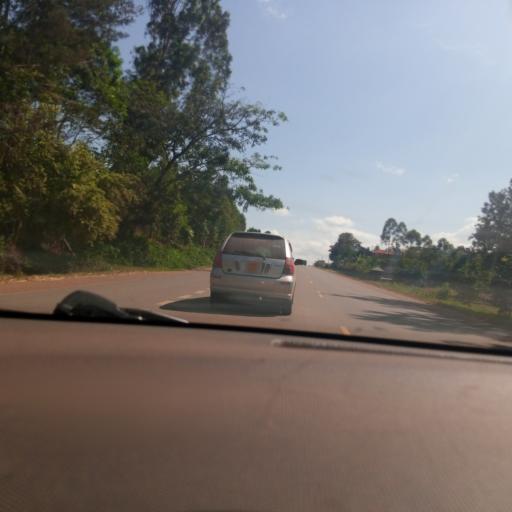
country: UG
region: Central Region
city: Masaka
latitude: -0.3115
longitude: 31.7502
